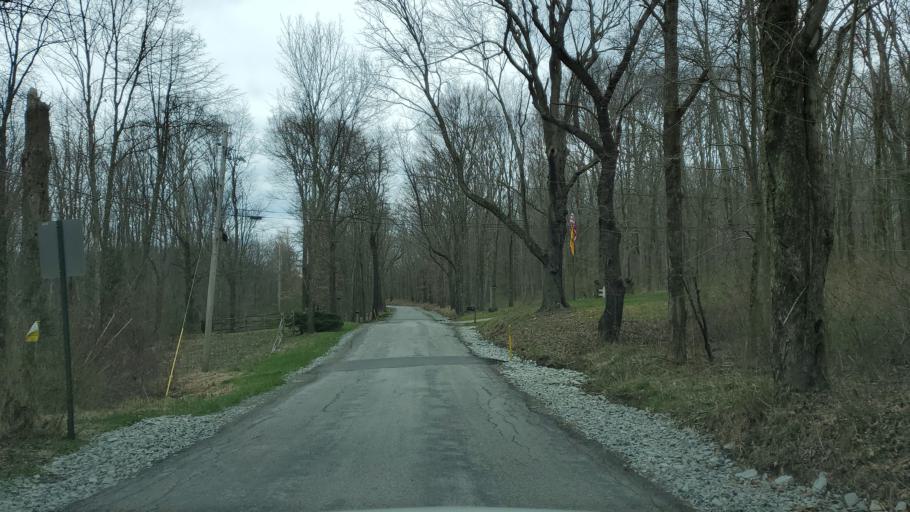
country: US
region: Pennsylvania
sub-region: Westmoreland County
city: Ligonier
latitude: 40.1729
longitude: -79.2604
